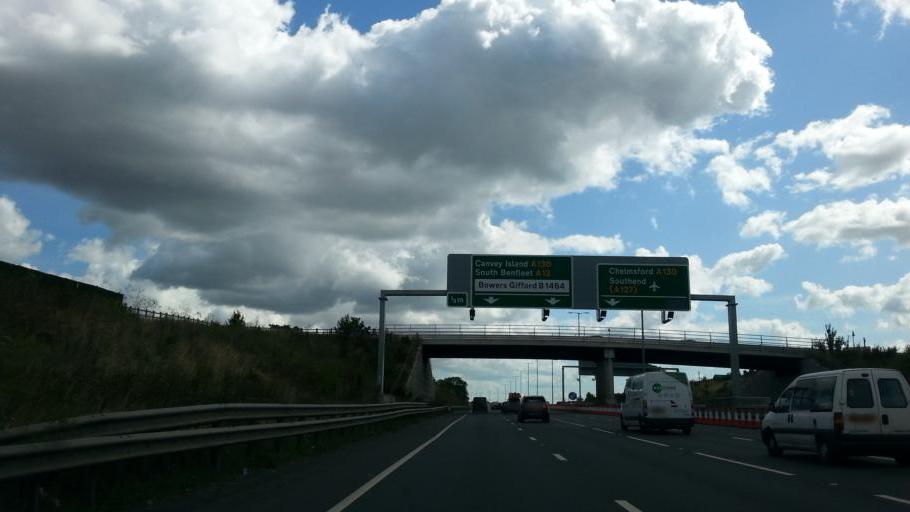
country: GB
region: England
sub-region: Essex
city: Pitsea
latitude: 51.5649
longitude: 0.5227
